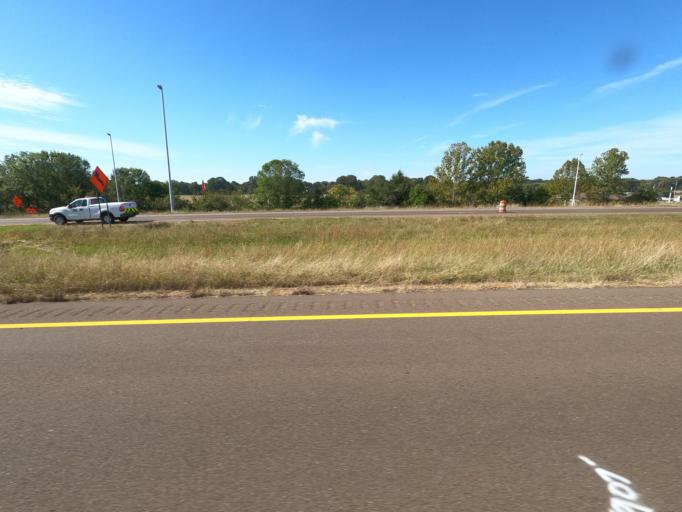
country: US
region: Tennessee
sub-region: Dyer County
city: Dyersburg
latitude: 36.0237
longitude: -89.3404
